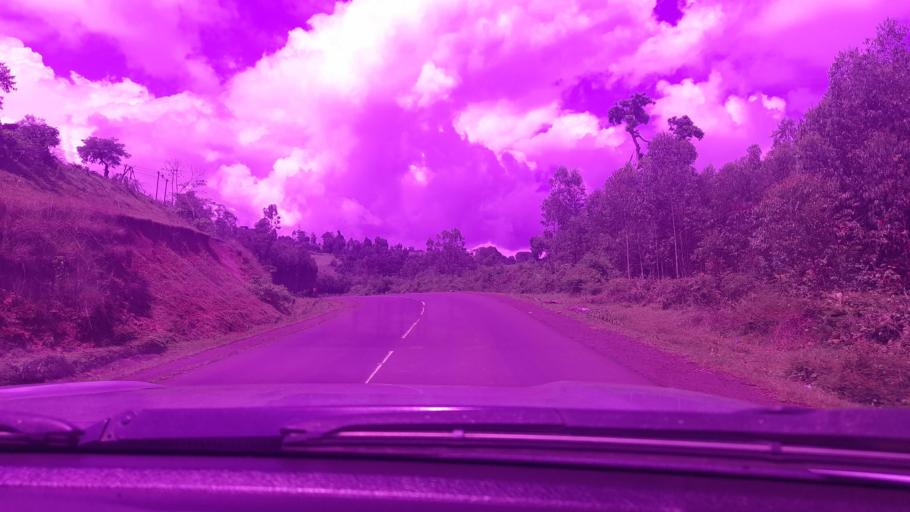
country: ET
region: Southern Nations, Nationalities, and People's Region
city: Bonga
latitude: 7.3878
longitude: 36.2927
